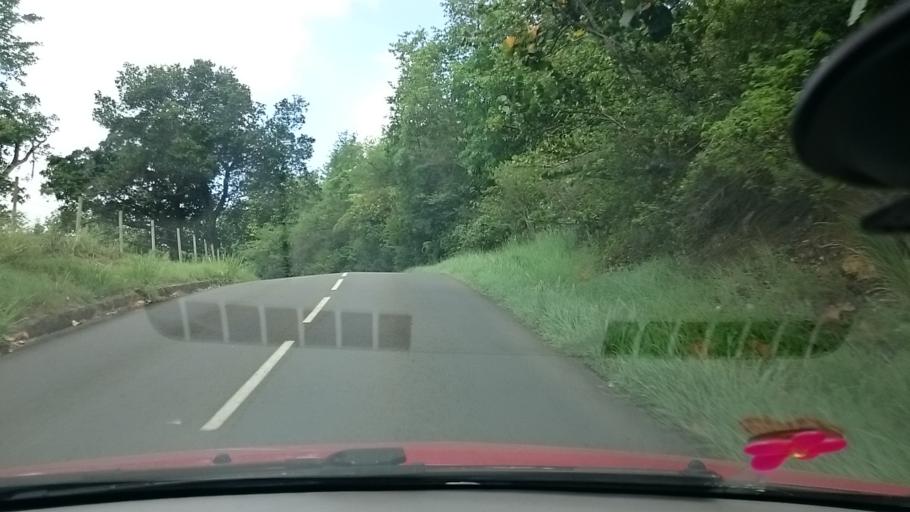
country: MQ
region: Martinique
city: Petite Riviere Salee
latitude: 14.7564
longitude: -60.9270
